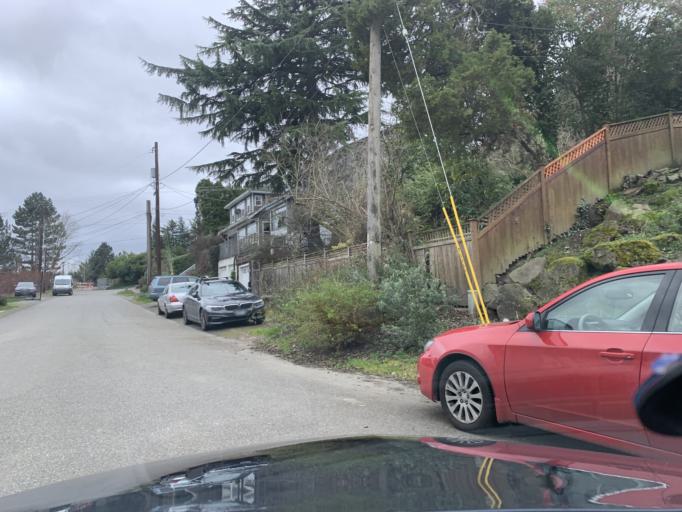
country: US
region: Washington
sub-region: King County
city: Seattle
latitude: 47.5919
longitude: -122.2880
